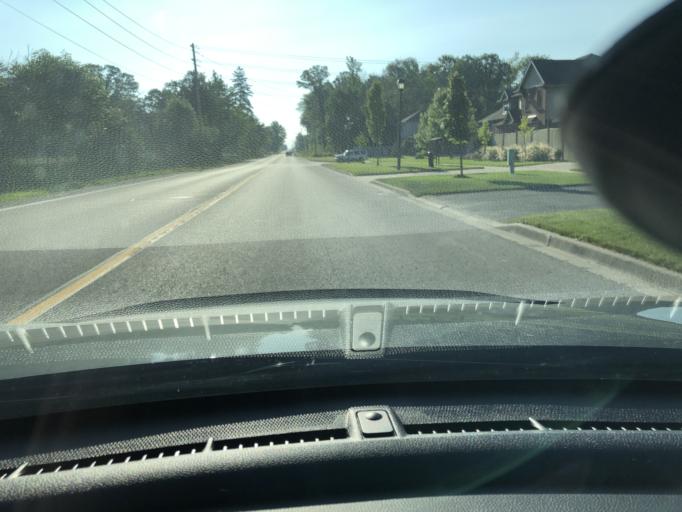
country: CA
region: Ontario
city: Stratford
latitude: 43.3893
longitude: -80.9595
